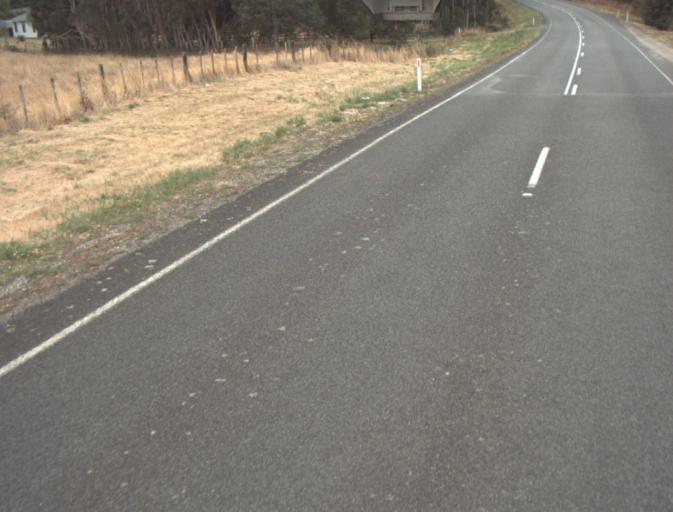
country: AU
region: Tasmania
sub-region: Launceston
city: Mayfield
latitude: -41.2775
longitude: 147.2199
